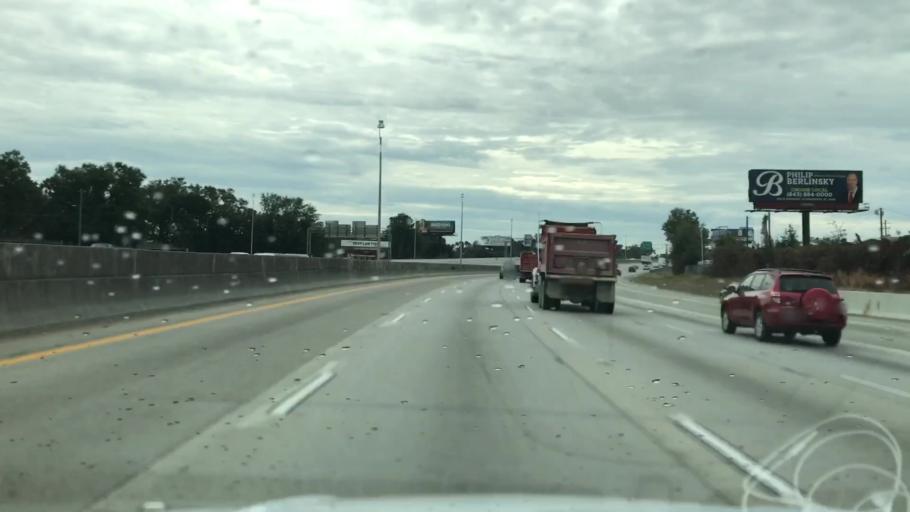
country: US
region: South Carolina
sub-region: Berkeley County
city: Hanahan
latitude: 32.8969
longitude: -80.0197
